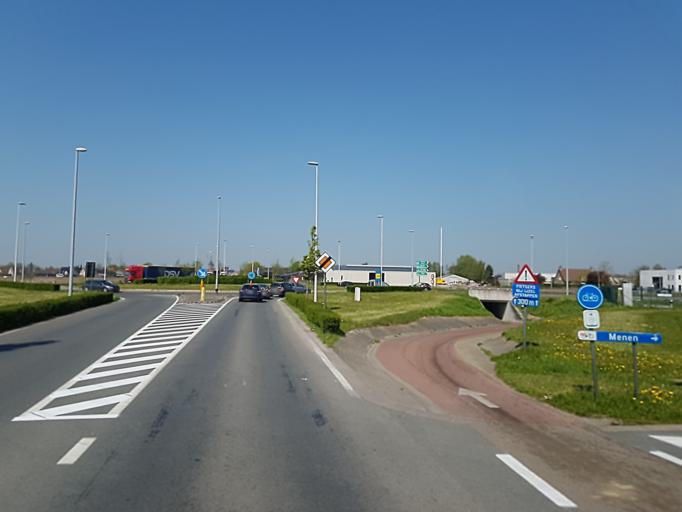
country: BE
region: Flanders
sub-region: Provincie West-Vlaanderen
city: Menen
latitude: 50.8063
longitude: 3.0902
